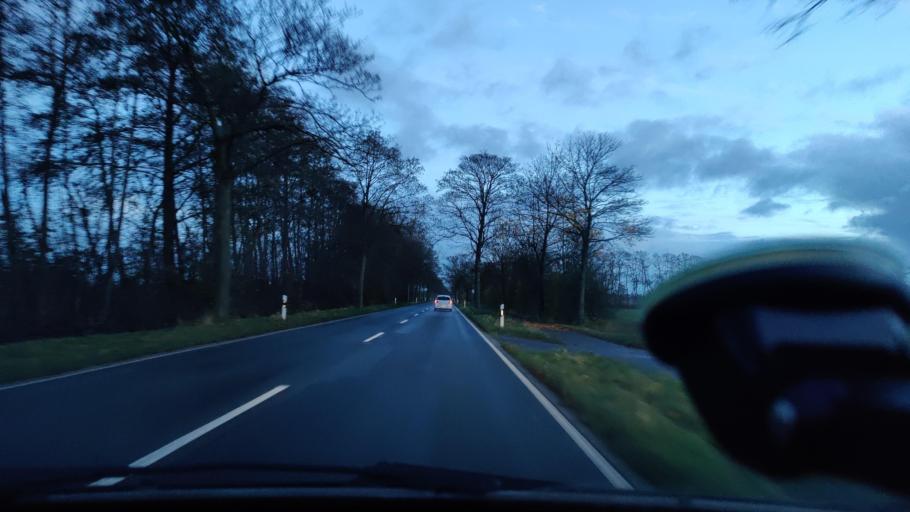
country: NL
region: Limburg
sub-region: Gemeente Bergen
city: Wellerlooi
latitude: 51.5795
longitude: 6.1380
